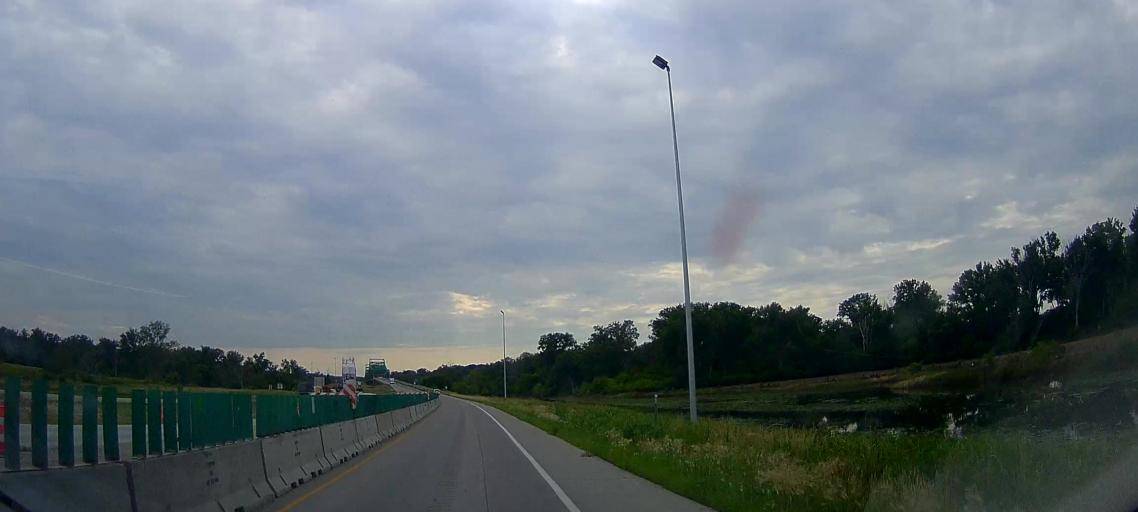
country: US
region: Iowa
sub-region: Pottawattamie County
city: Carter Lake
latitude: 41.3468
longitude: -95.9495
